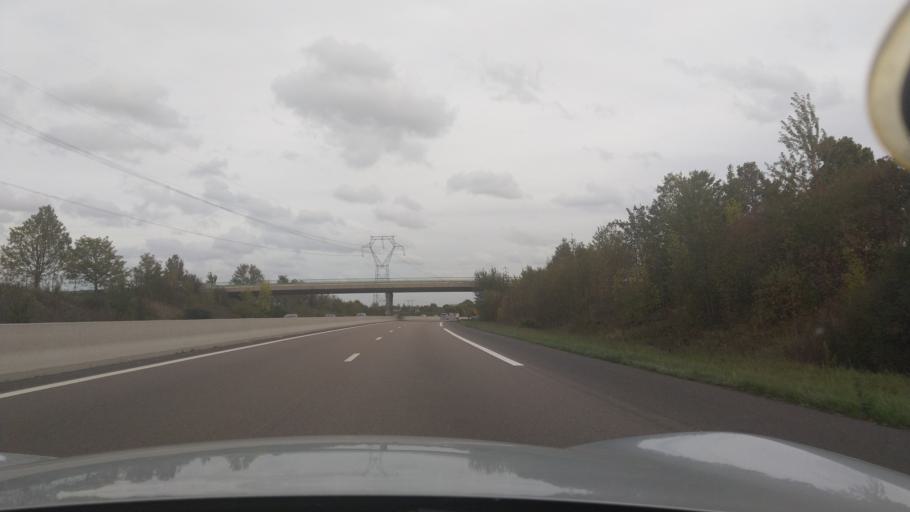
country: FR
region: Ile-de-France
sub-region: Departement du Val-d'Oise
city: Puiseux-en-France
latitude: 49.0439
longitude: 2.4775
